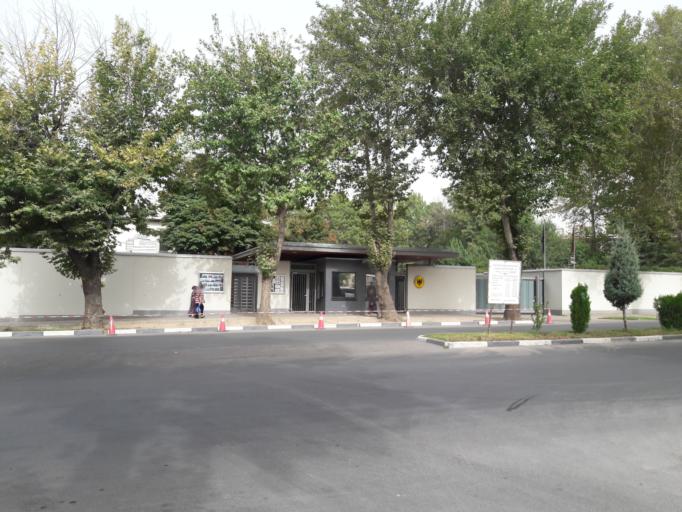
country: TJ
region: Dushanbe
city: Dushanbe
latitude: 38.5807
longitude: 68.7492
